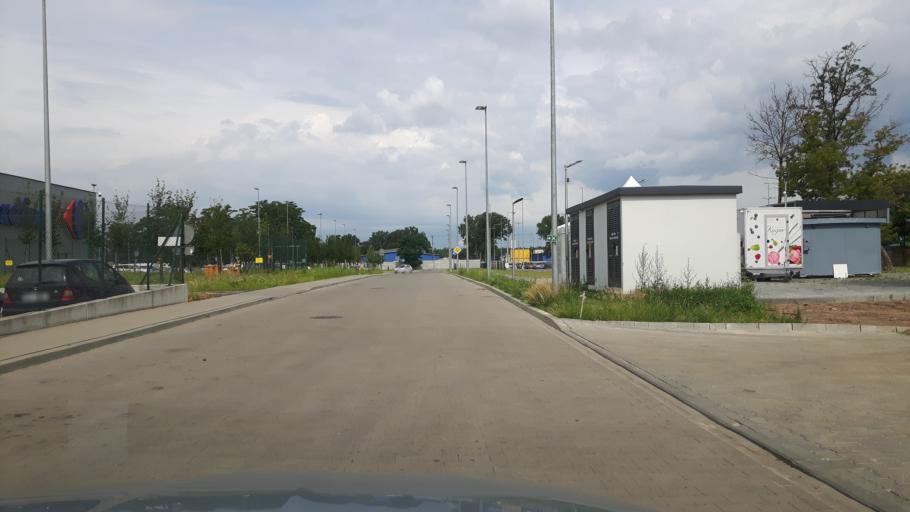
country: PL
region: Masovian Voivodeship
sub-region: Powiat wolominski
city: Nowe Lipiny
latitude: 52.3573
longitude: 21.2602
